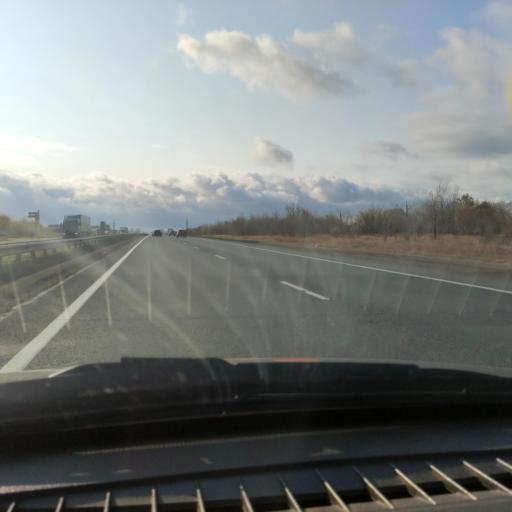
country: RU
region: Samara
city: Tol'yatti
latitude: 53.5673
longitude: 49.3751
